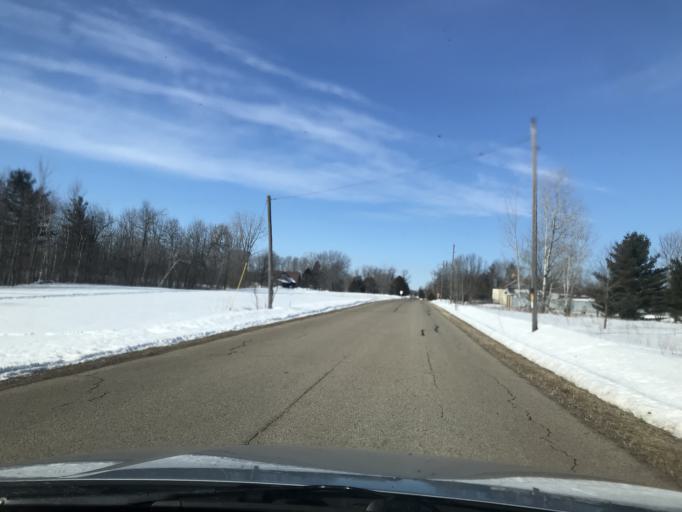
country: US
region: Wisconsin
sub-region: Oconto County
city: Oconto Falls
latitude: 44.9231
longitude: -88.1623
